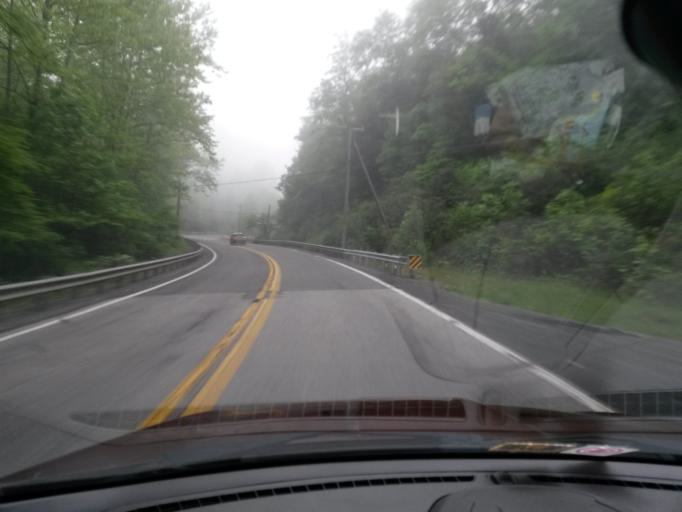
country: US
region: West Virginia
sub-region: Wyoming County
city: Pineville
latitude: 37.5026
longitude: -81.5434
